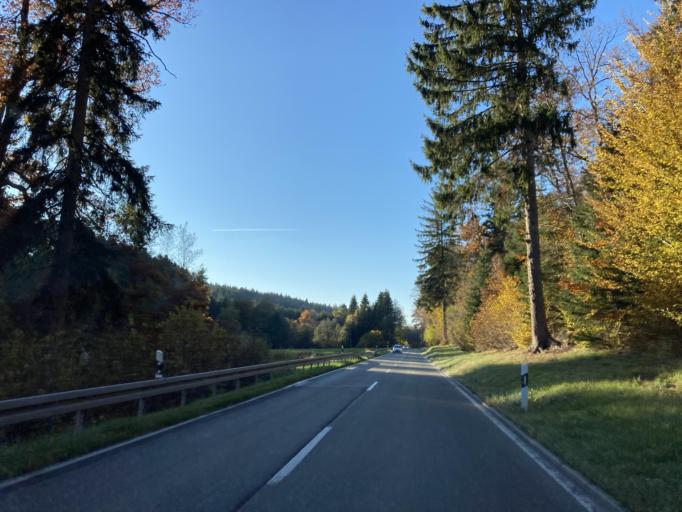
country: DE
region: Baden-Wuerttemberg
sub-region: Tuebingen Region
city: Bodelshausen
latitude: 48.4249
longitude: 8.9801
